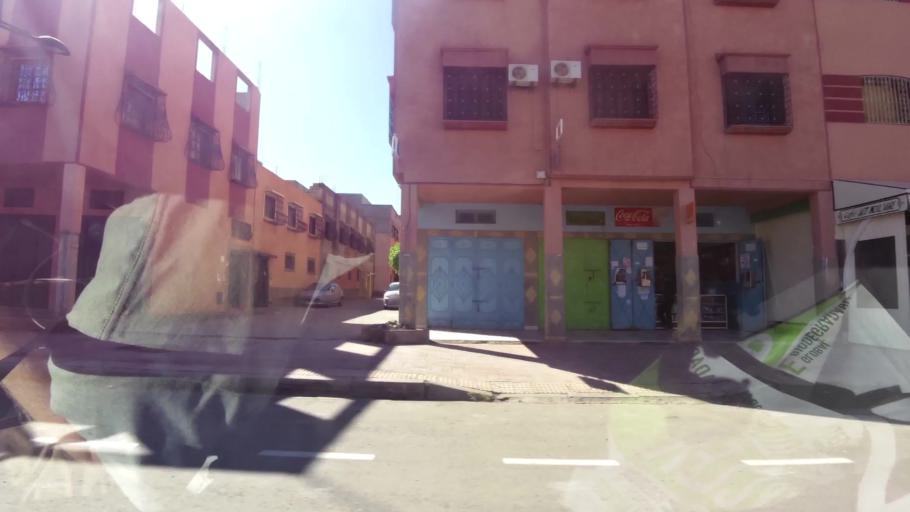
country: MA
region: Marrakech-Tensift-Al Haouz
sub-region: Marrakech
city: Marrakesh
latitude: 31.5907
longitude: -8.0513
